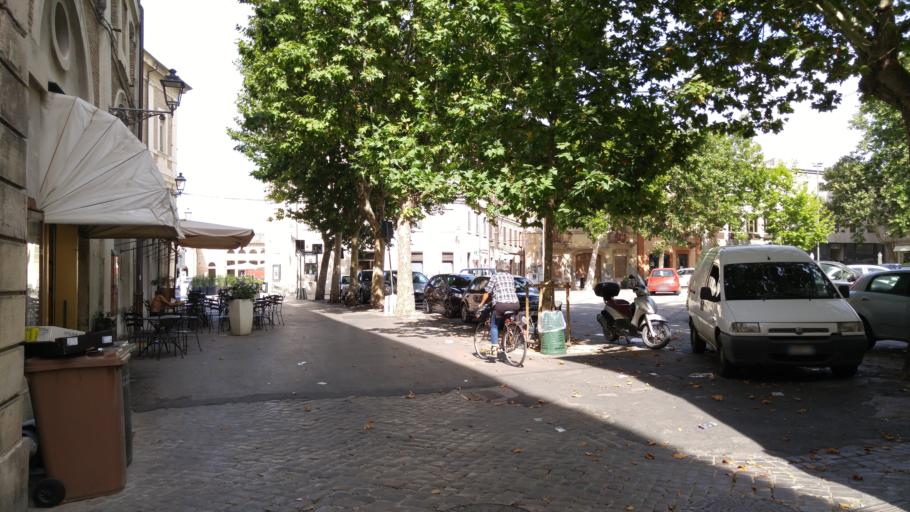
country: IT
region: The Marches
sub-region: Provincia di Ancona
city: Senigallia
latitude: 43.7157
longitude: 13.2182
